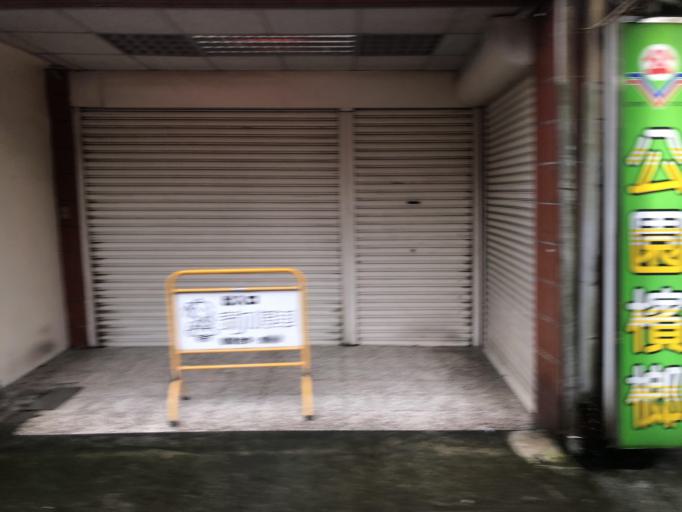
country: TW
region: Taipei
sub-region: Taipei
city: Banqiao
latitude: 24.9570
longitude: 121.4156
